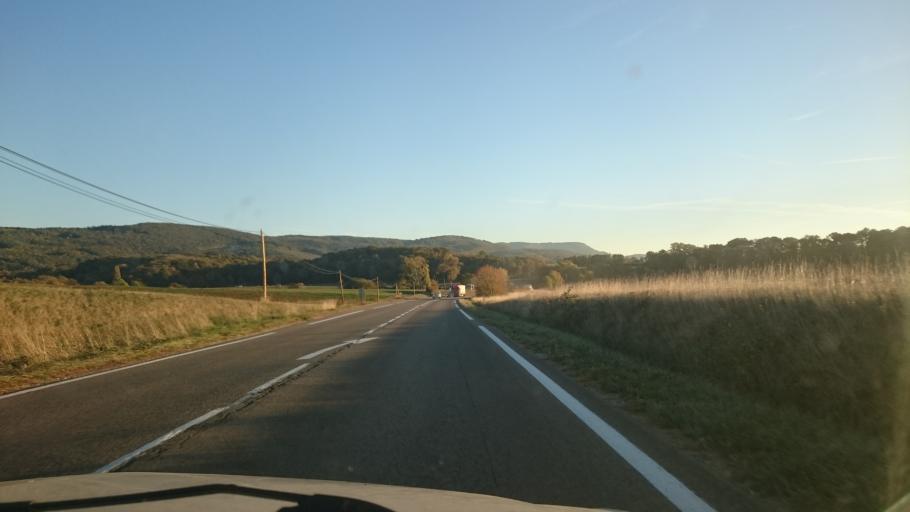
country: FR
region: Franche-Comte
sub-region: Departement du Doubs
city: Quingey
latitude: 47.0628
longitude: 5.8824
